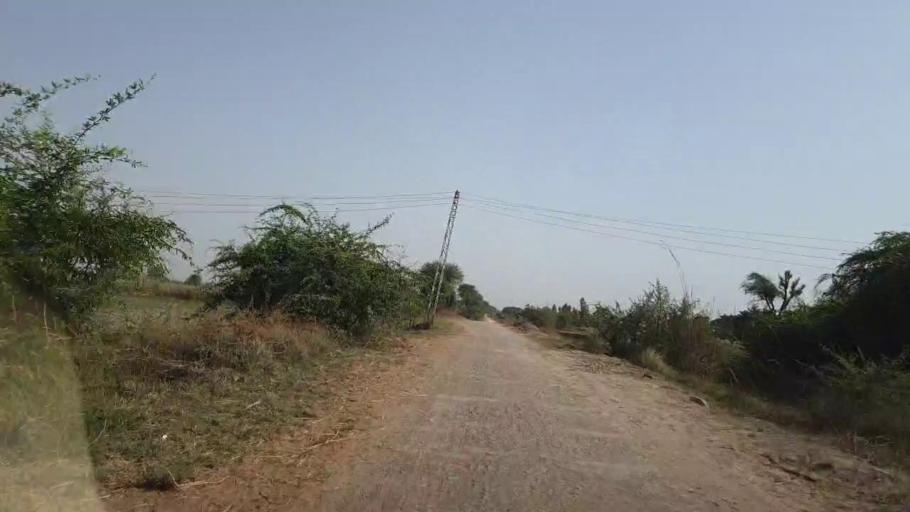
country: PK
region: Sindh
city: Rajo Khanani
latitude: 25.0469
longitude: 68.8369
